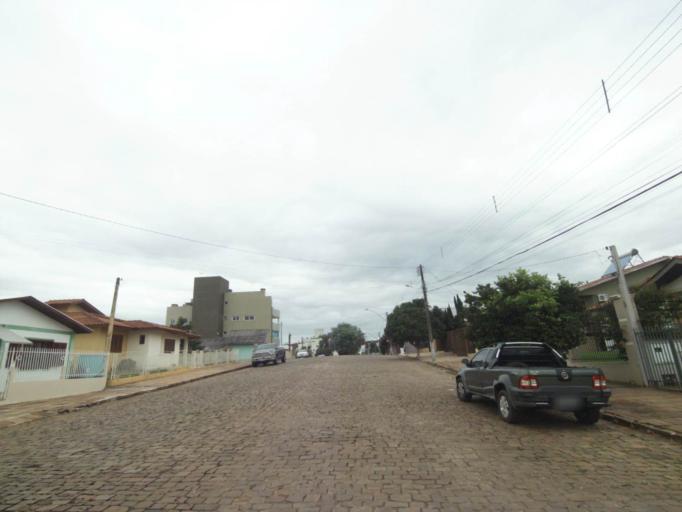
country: BR
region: Rio Grande do Sul
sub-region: Lagoa Vermelha
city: Lagoa Vermelha
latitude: -28.2144
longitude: -51.5249
